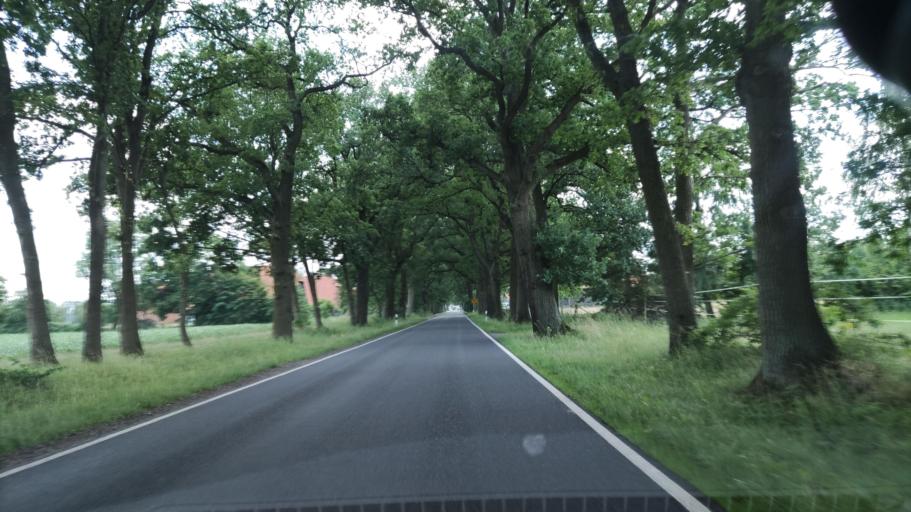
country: DE
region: Mecklenburg-Vorpommern
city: Lubtheen
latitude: 53.3432
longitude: 11.1429
